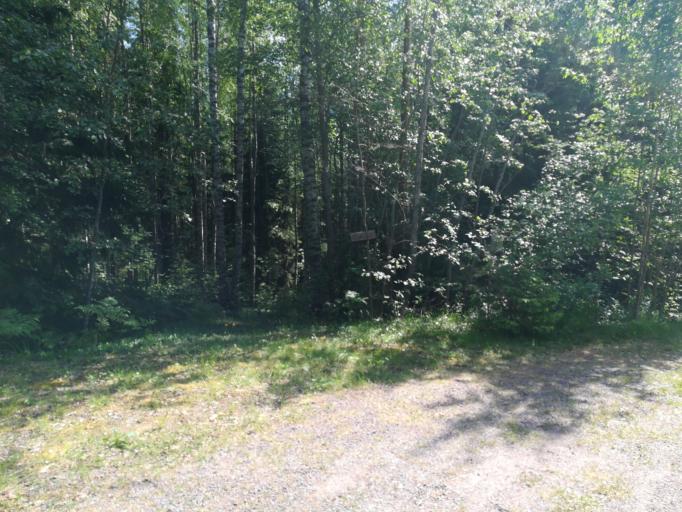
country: FI
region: South Karelia
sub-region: Imatra
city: Ruokolahti
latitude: 61.4818
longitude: 28.8703
